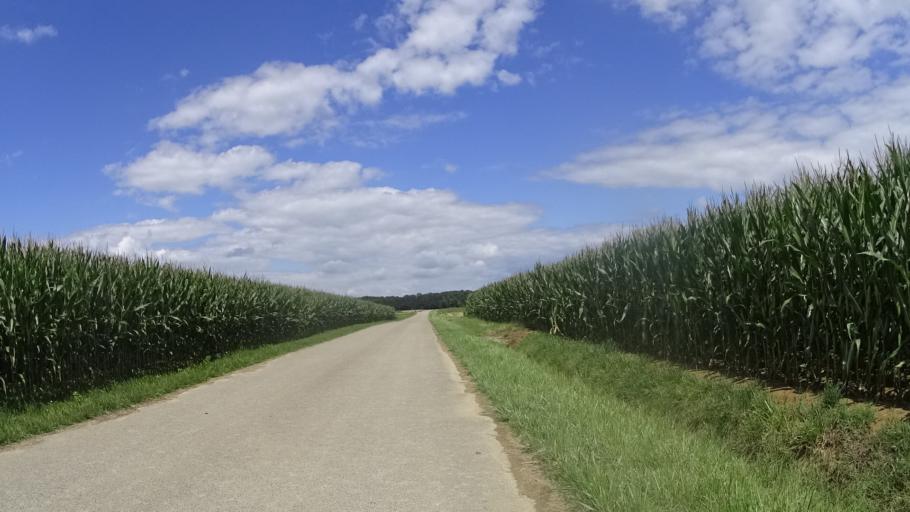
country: FR
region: Champagne-Ardenne
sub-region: Departement de la Haute-Marne
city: Montier-en-Der
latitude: 48.5139
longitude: 4.7747
